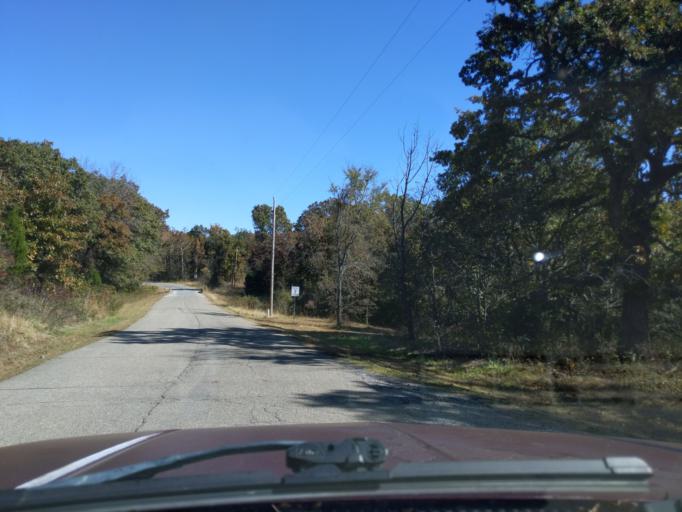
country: US
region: Oklahoma
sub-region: Creek County
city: Bristow
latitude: 35.7049
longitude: -96.4064
